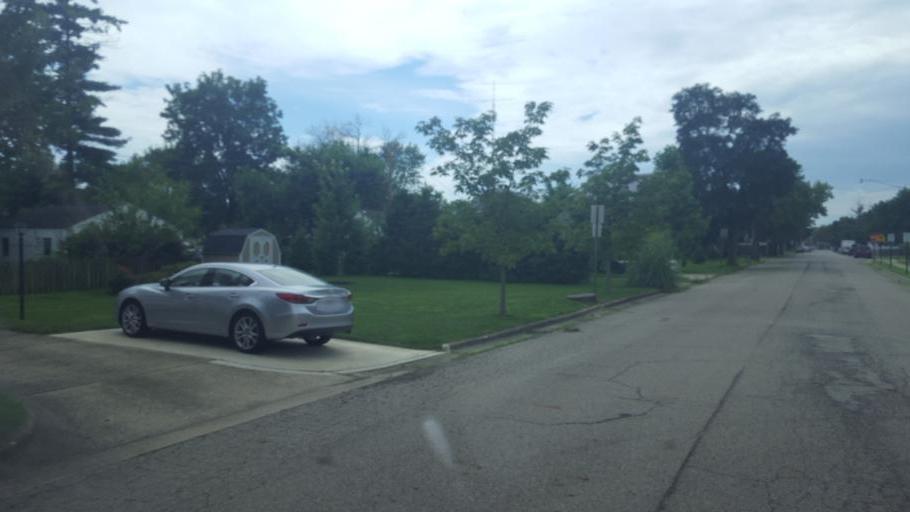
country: US
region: Ohio
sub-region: Pickaway County
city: Ashville
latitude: 39.7152
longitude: -82.9485
